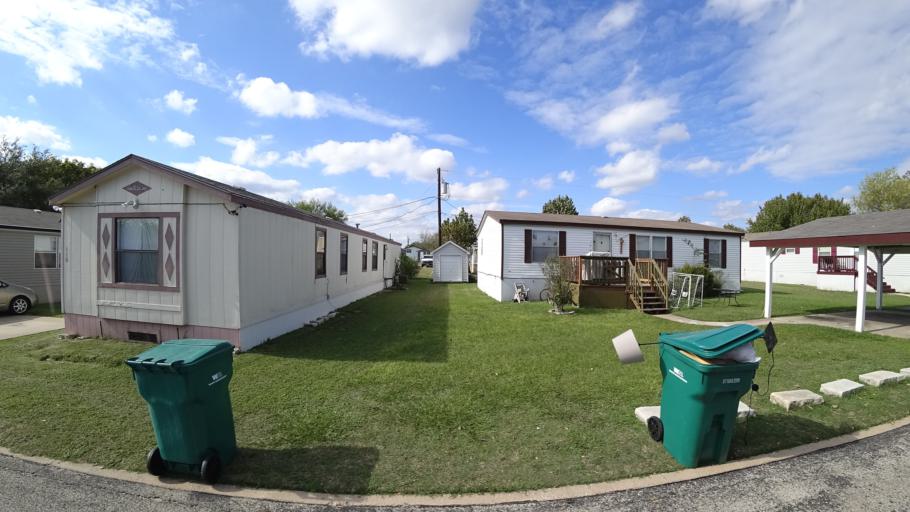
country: US
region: Texas
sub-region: Travis County
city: Pflugerville
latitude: 30.4324
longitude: -97.6399
